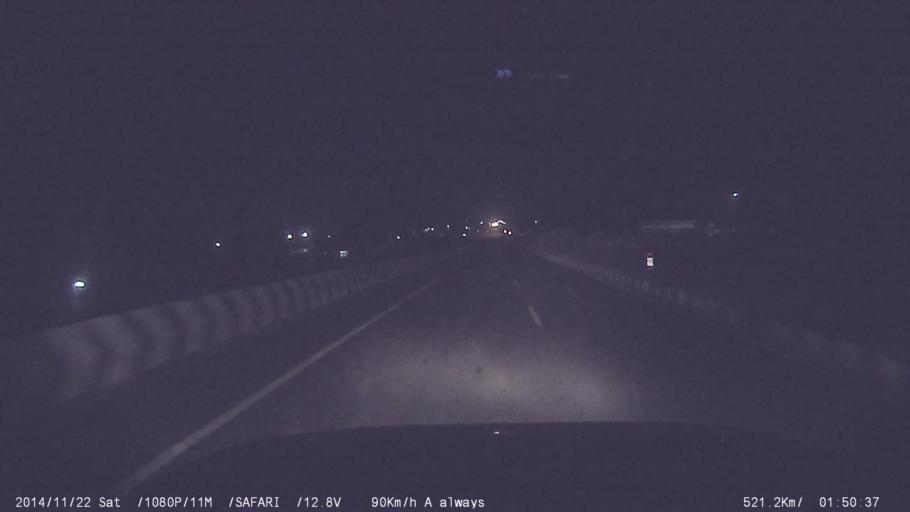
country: IN
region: Tamil Nadu
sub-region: Villupuram
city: Chinna Salem
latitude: 11.6240
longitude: 78.8563
